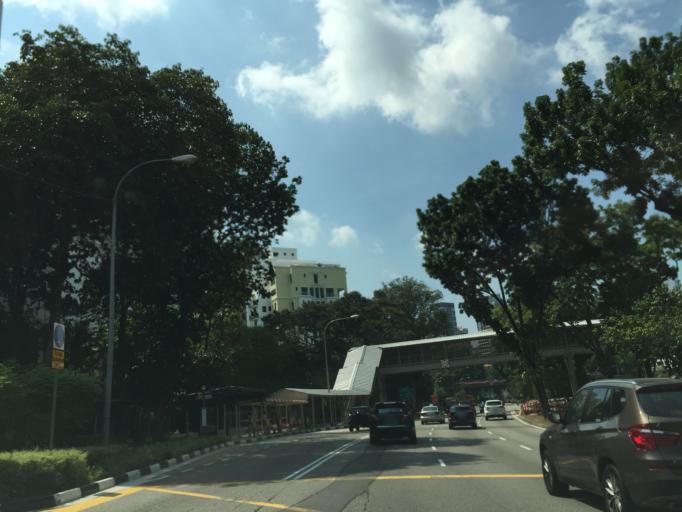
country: SG
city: Singapore
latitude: 1.3068
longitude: 103.8197
